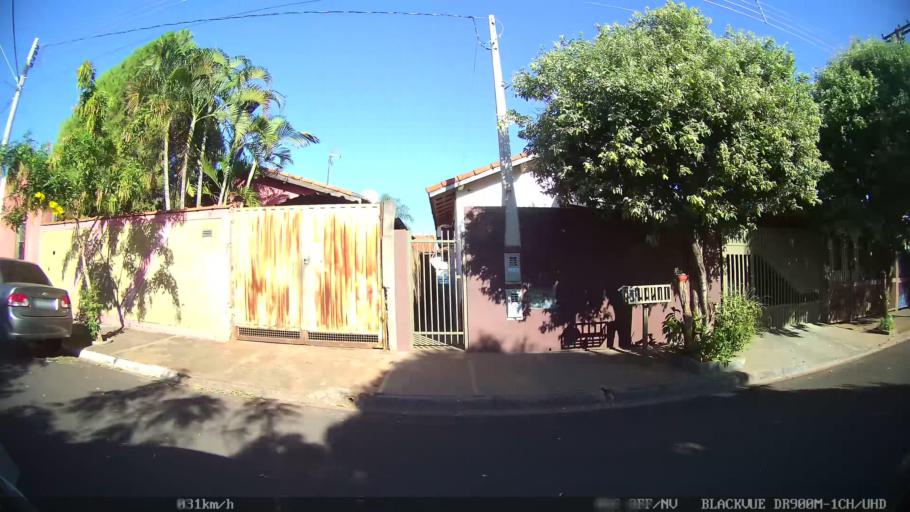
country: BR
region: Sao Paulo
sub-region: Olimpia
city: Olimpia
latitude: -20.7263
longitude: -48.8980
